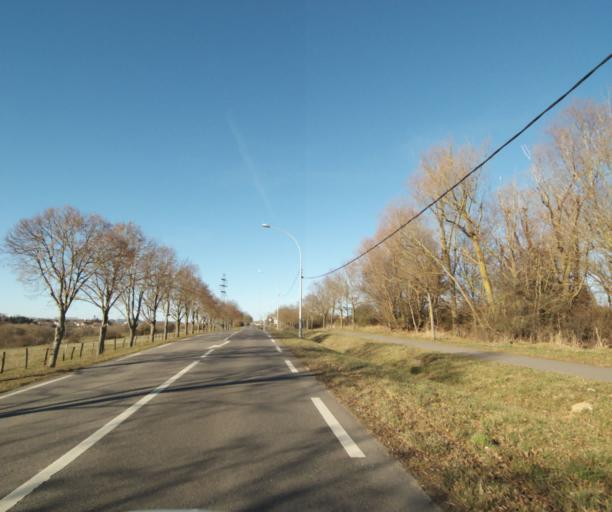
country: FR
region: Lorraine
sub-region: Departement de Meurthe-et-Moselle
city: Heillecourt
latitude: 48.6536
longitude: 6.2074
